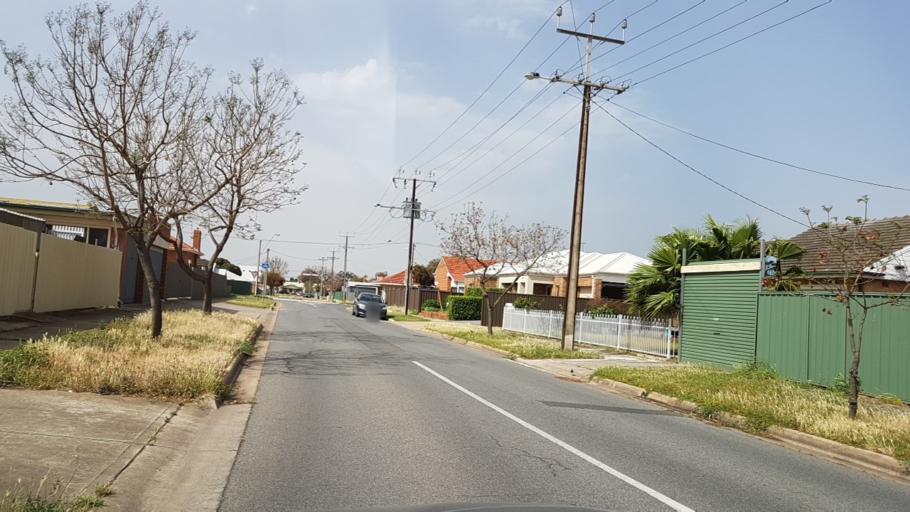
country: AU
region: South Australia
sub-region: Charles Sturt
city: Seaton
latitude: -34.8889
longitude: 138.5196
